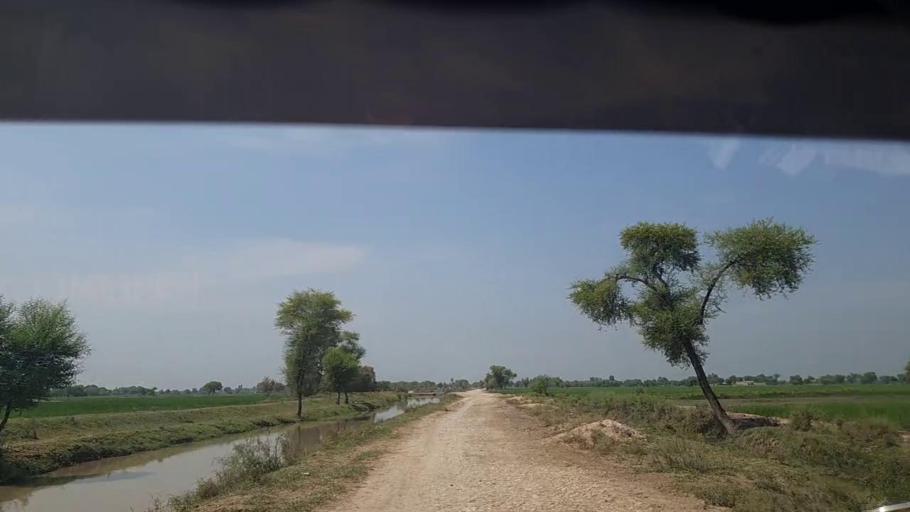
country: PK
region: Sindh
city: Thul
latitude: 28.1941
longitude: 68.7089
